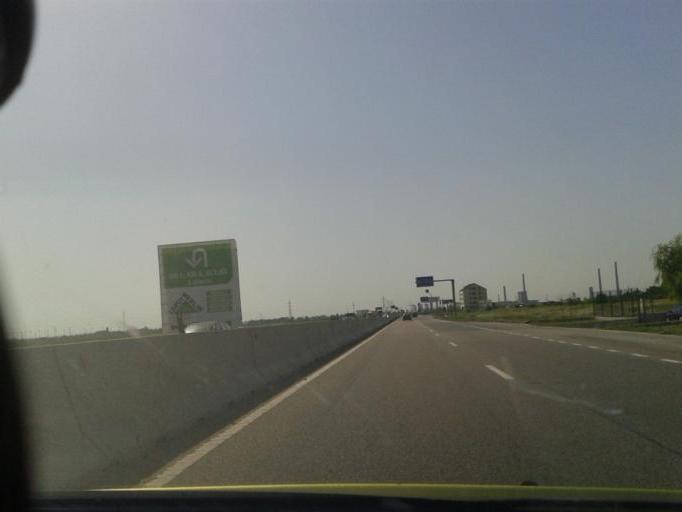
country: RO
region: Prahova
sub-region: Comuna Targsoru Vechi
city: Strejnicu
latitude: 44.9143
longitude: 25.9892
